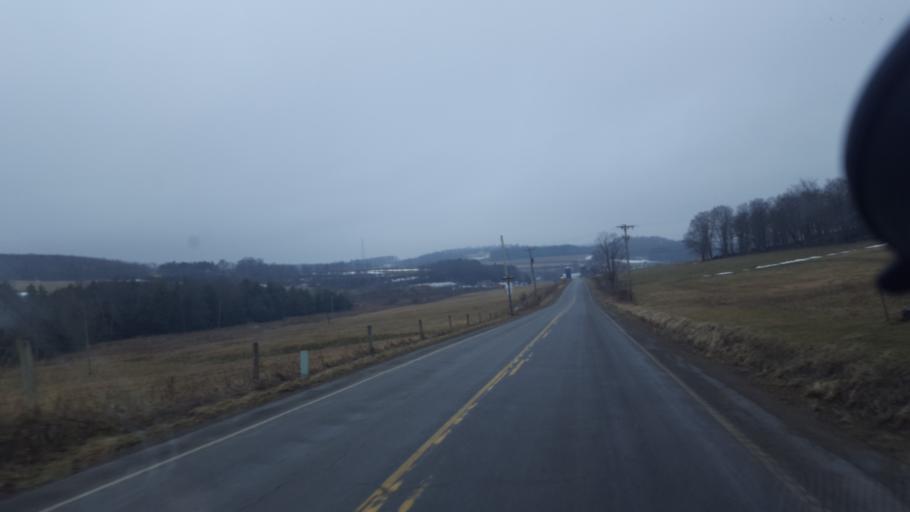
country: US
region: Pennsylvania
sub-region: Tioga County
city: Westfield
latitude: 41.9235
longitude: -77.7355
